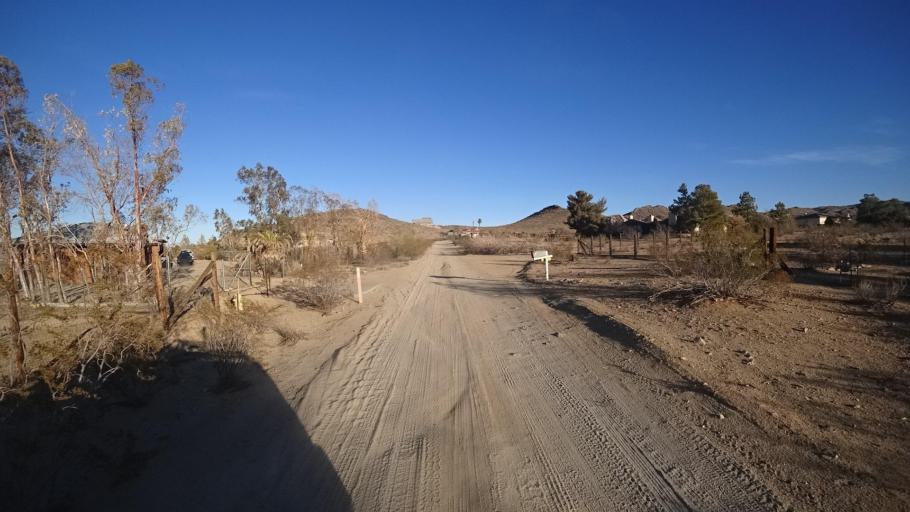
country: US
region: California
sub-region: Kern County
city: Ridgecrest
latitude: 35.5824
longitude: -117.6547
